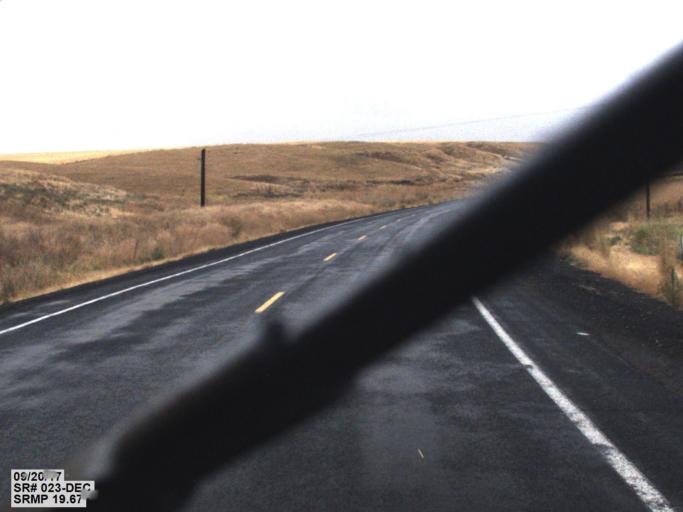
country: US
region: Washington
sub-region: Spokane County
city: Cheney
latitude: 47.1180
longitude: -117.6841
